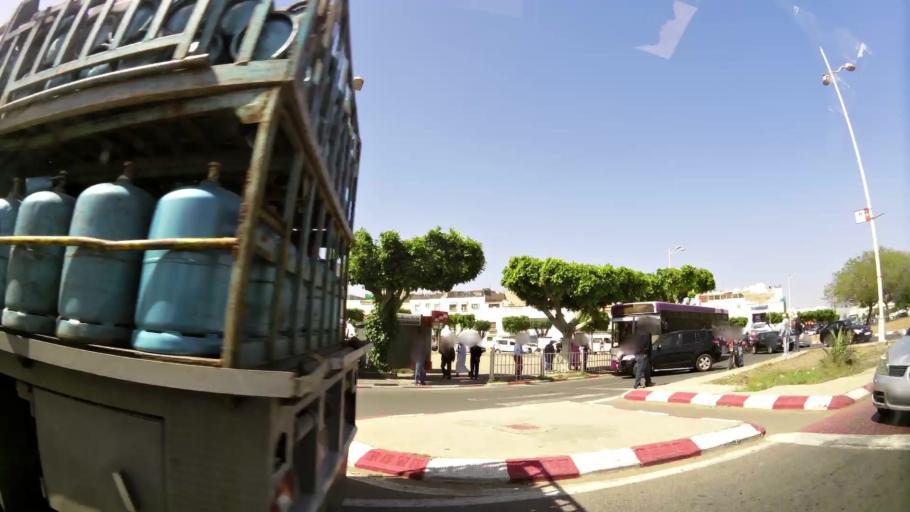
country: MA
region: Oued ed Dahab-Lagouira
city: Dakhla
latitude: 30.4144
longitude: -9.5699
